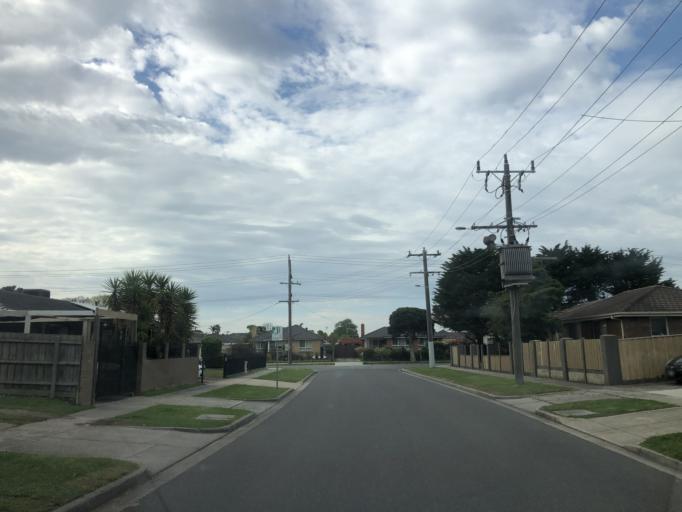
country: AU
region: Victoria
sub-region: Casey
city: Hampton Park
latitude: -38.0348
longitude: 145.2563
